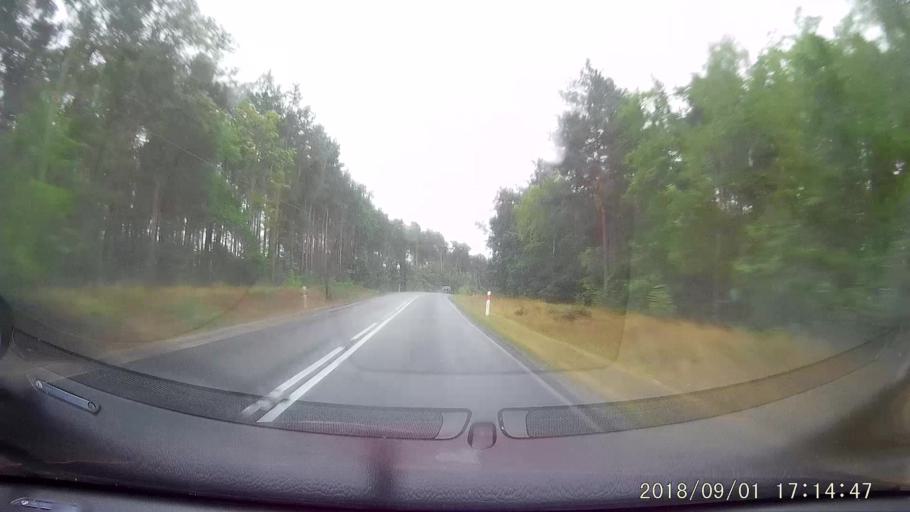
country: PL
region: Lubusz
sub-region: Powiat zielonogorski
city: Nowogrod Bobrzanski
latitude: 51.7811
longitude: 15.2608
